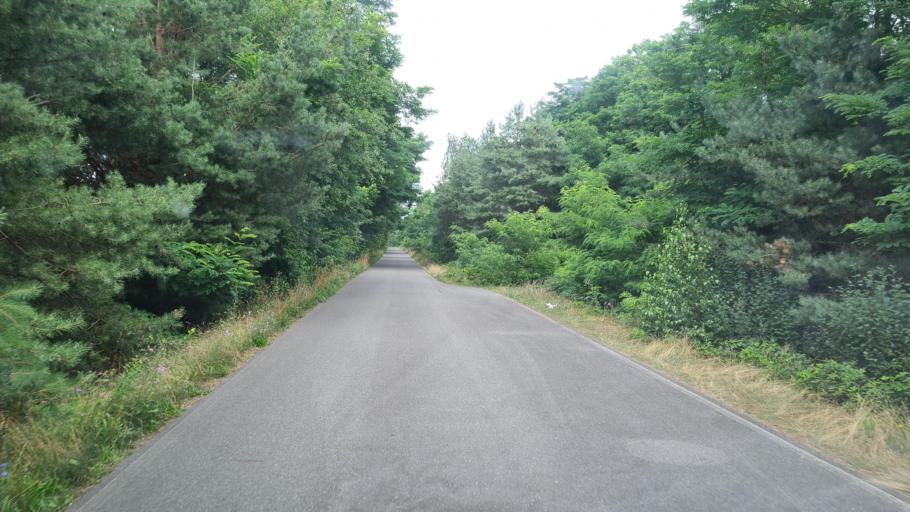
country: DE
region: Brandenburg
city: Neupetershain
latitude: 51.6744
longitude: 14.1156
